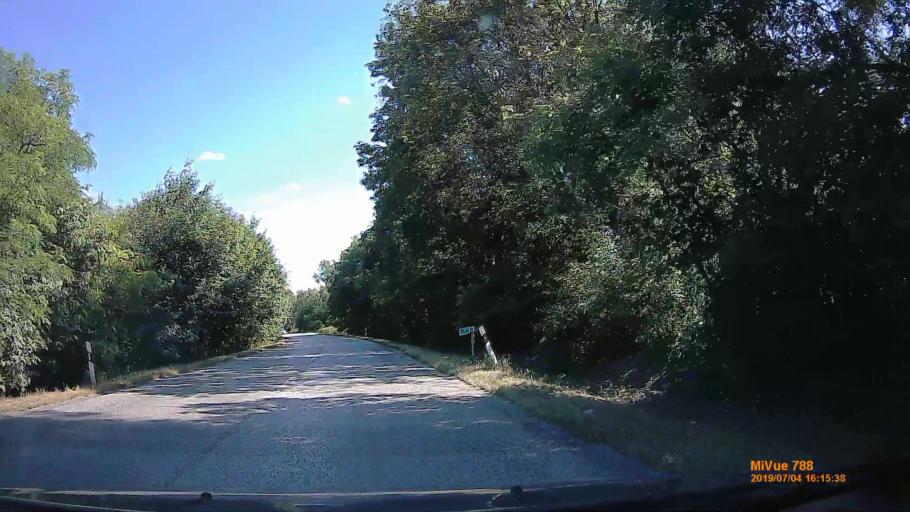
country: HU
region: Fejer
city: Etyek
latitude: 47.4984
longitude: 18.7604
